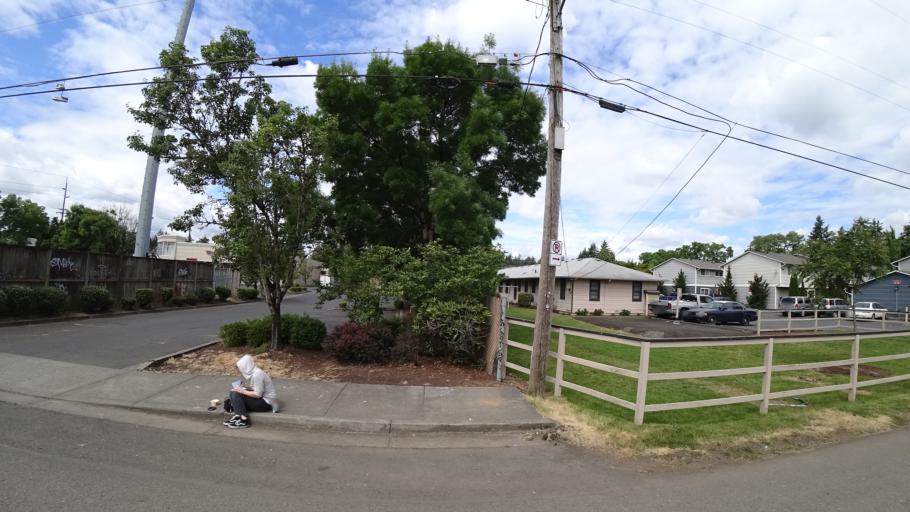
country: US
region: Oregon
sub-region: Multnomah County
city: Lents
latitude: 45.4978
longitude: -122.5359
